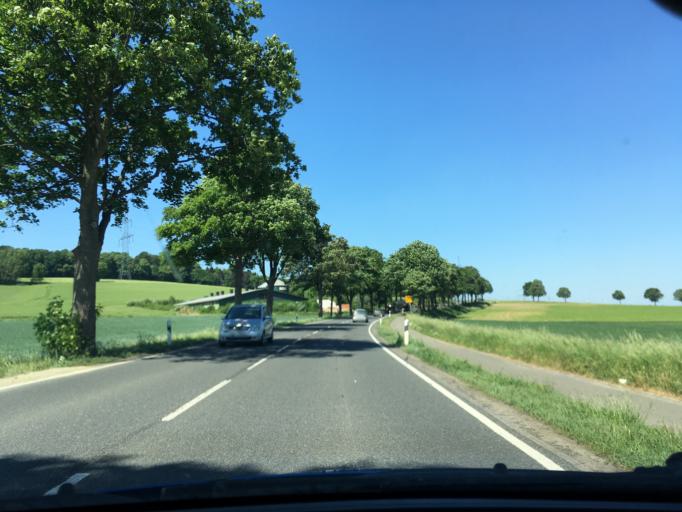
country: DE
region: Lower Saxony
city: Beckedorf
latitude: 52.3313
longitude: 9.3358
